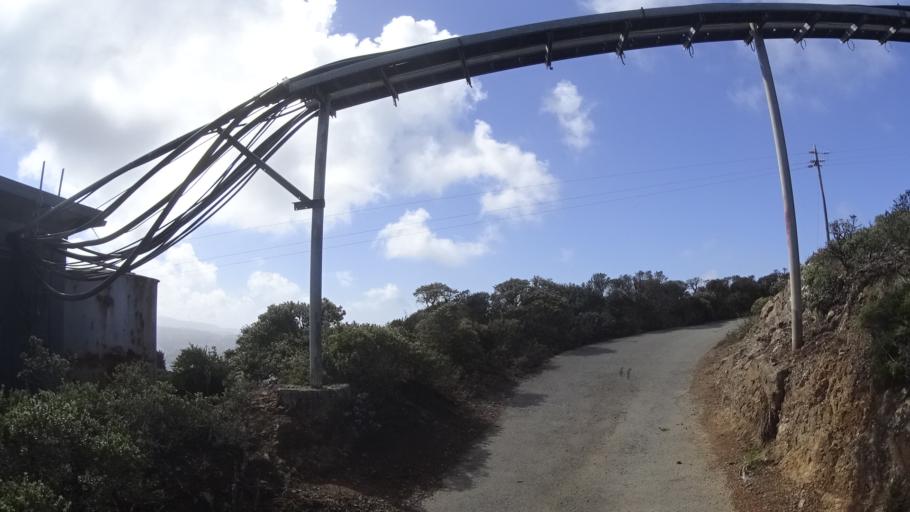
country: US
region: California
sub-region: San Mateo County
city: Colma
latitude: 37.6890
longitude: -122.4373
